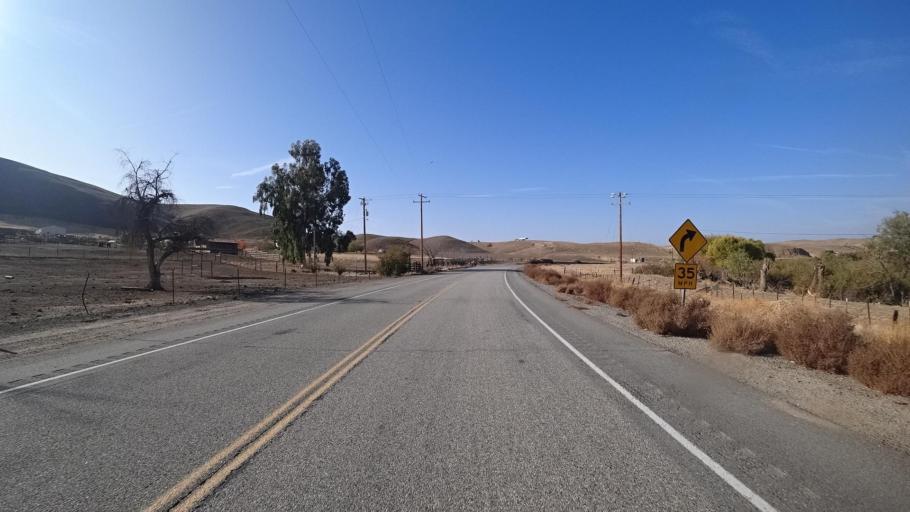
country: US
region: California
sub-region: Kern County
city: Oildale
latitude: 35.5276
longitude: -118.9686
